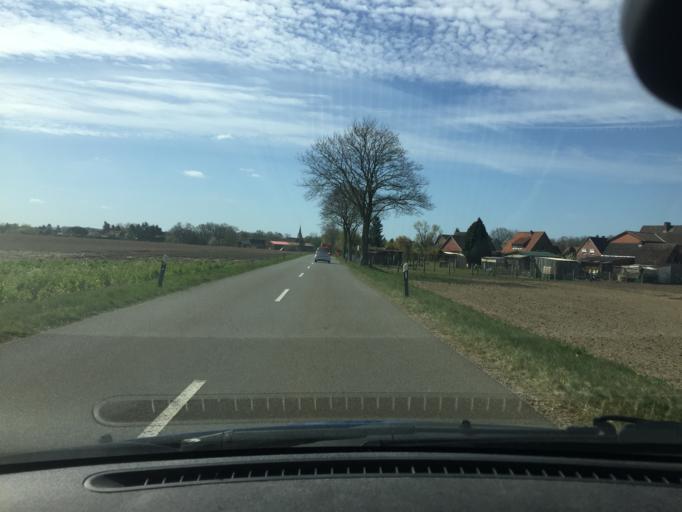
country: DE
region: Lower Saxony
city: Ratzlingen
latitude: 52.9347
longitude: 10.6471
